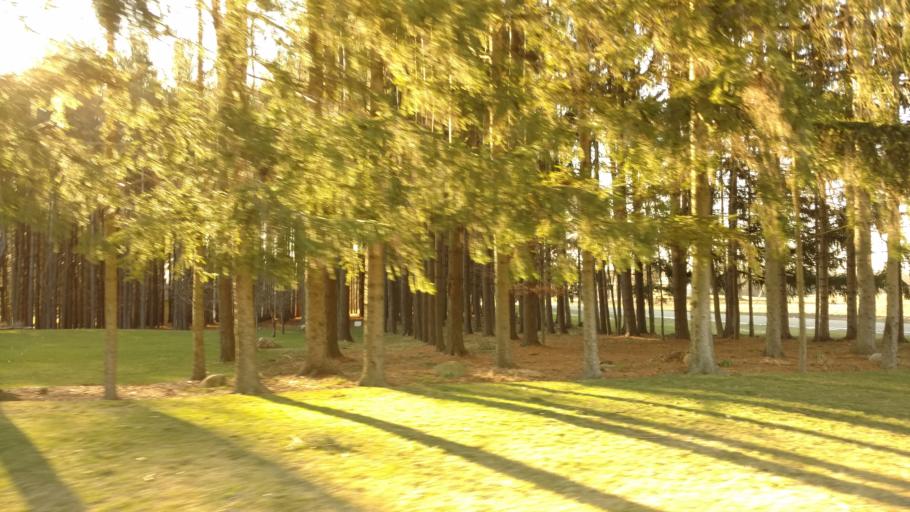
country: US
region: Ohio
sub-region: Richland County
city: Ontario
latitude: 40.7464
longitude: -82.6087
